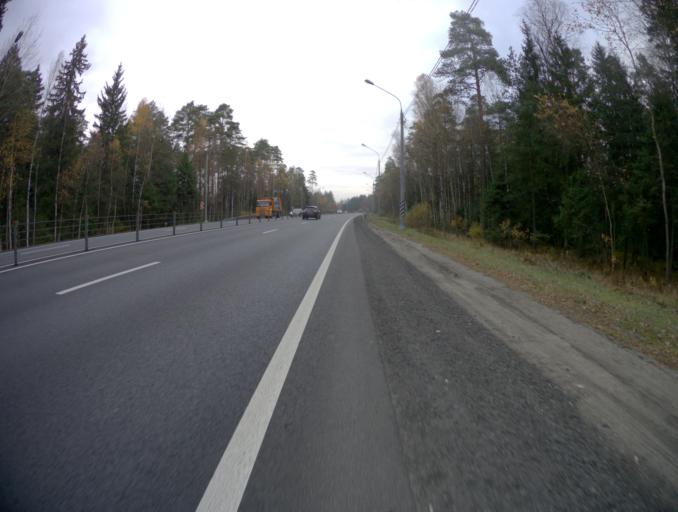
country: RU
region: Moskovskaya
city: Malaya Dubna
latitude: 55.8647
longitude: 38.9630
